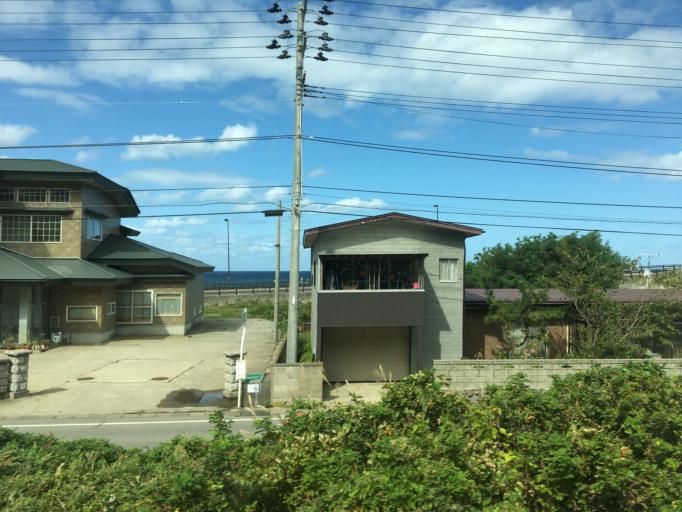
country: JP
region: Aomori
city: Shimokizukuri
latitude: 40.7693
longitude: 140.1705
